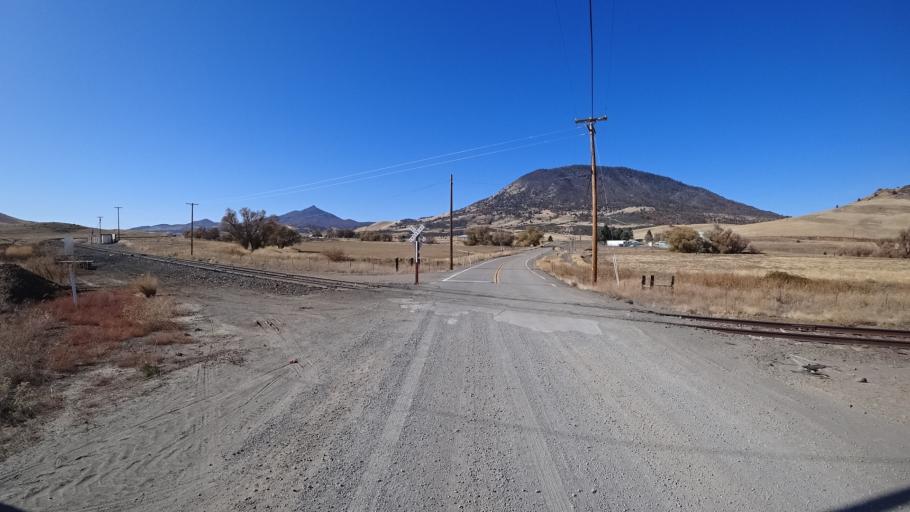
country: US
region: California
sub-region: Siskiyou County
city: Montague
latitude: 41.8479
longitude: -122.4650
